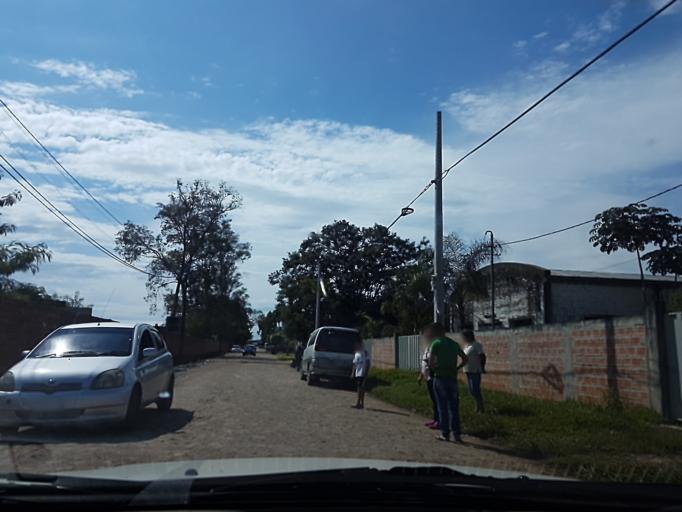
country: PY
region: Central
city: Colonia Mariano Roque Alonso
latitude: -25.2027
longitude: -57.5322
